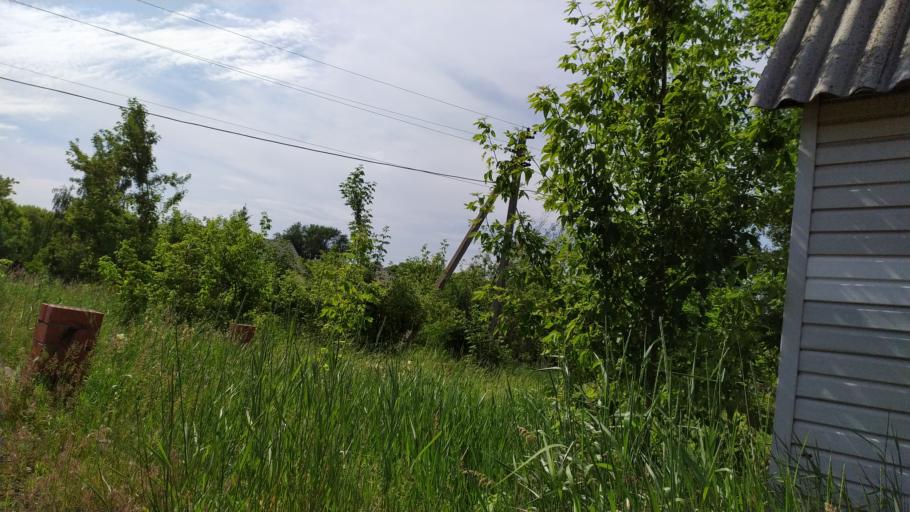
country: RU
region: Kursk
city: Kursk
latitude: 51.6598
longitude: 36.1528
